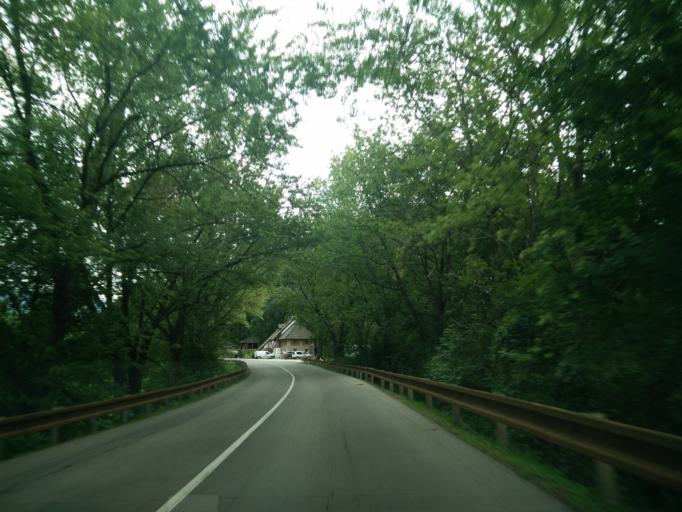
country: SK
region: Nitriansky
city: Novaky
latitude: 48.6008
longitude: 18.5016
